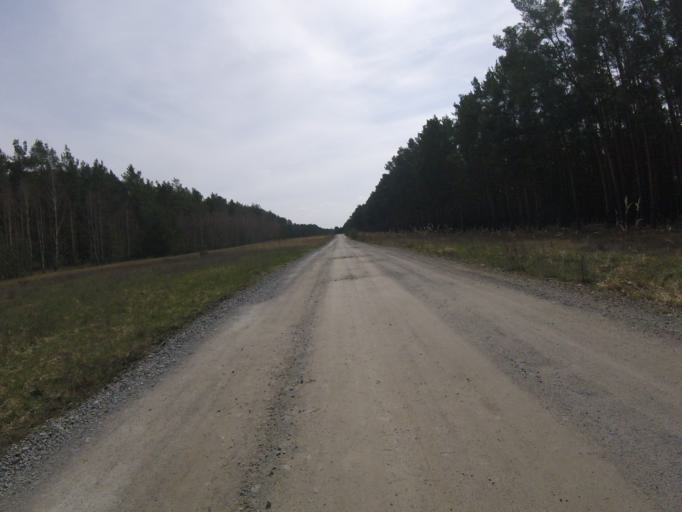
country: DE
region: Brandenburg
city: Schwerin
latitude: 52.1873
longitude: 13.6248
